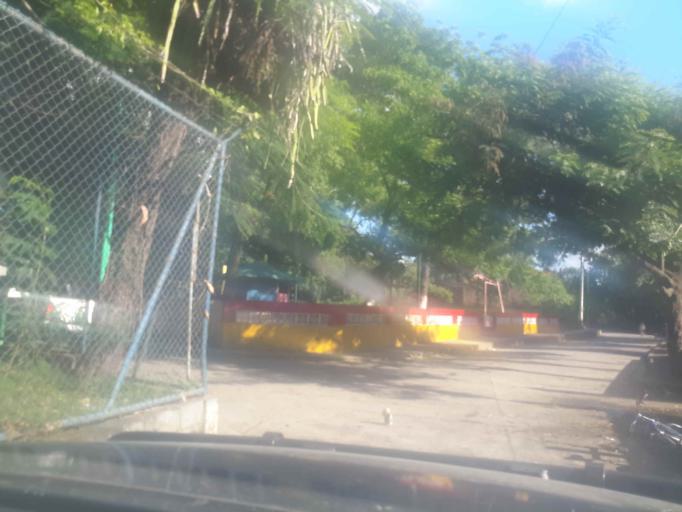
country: NI
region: Rivas
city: Moyogalpa
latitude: 11.5566
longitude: -85.6748
